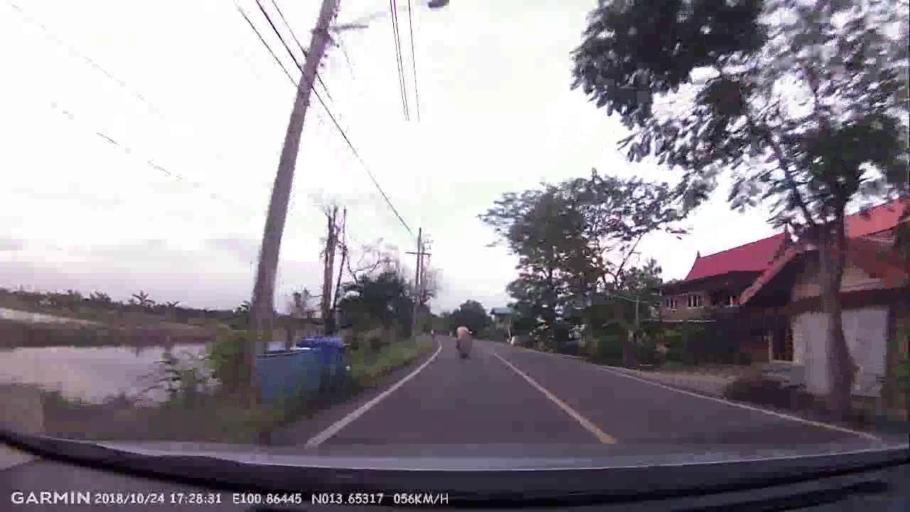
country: TH
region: Samut Prakan
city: Ban Khlong Bang Sao Thong
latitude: 13.6534
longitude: 100.8645
